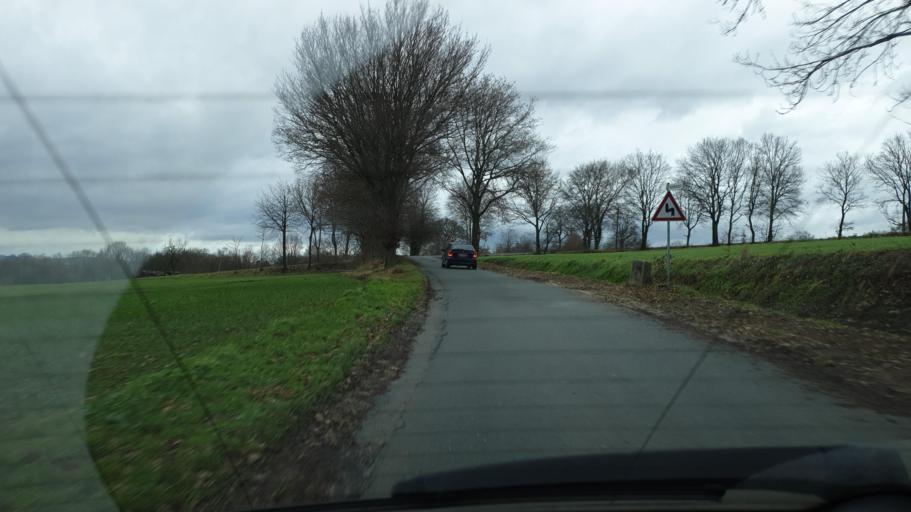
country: DE
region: North Rhine-Westphalia
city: Bad Oeynhausen
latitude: 52.1661
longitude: 8.7742
